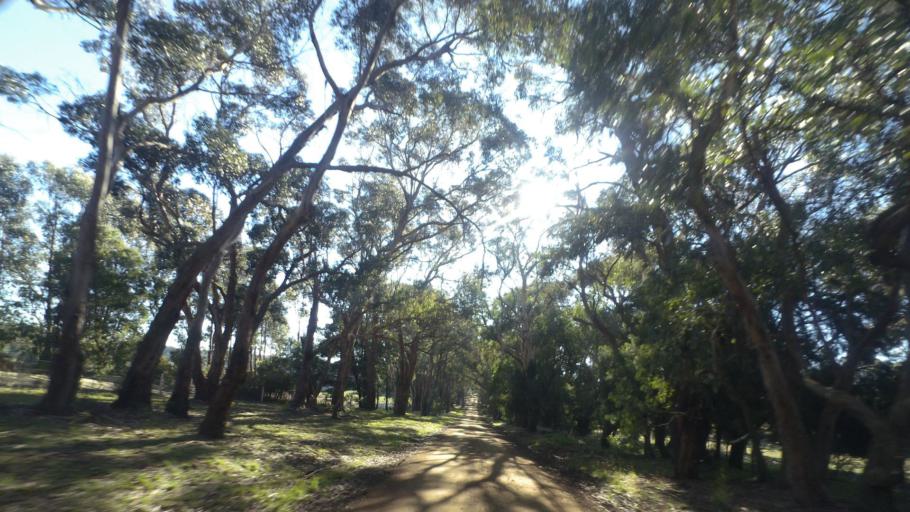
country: AU
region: Victoria
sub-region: Mount Alexander
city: Castlemaine
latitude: -37.2963
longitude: 144.3327
